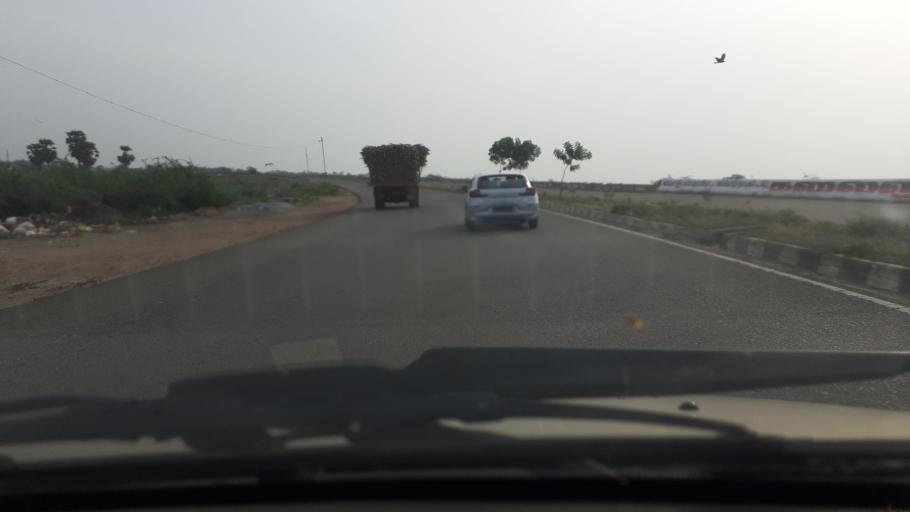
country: IN
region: Tamil Nadu
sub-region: Thoothukkudi
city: Korampallam
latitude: 8.7542
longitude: 78.0591
